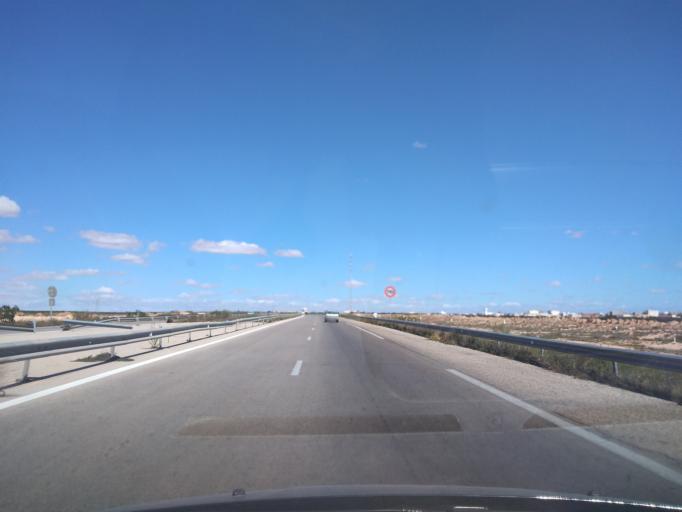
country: TN
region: Safaqis
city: Al Qarmadah
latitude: 34.9320
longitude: 10.7381
